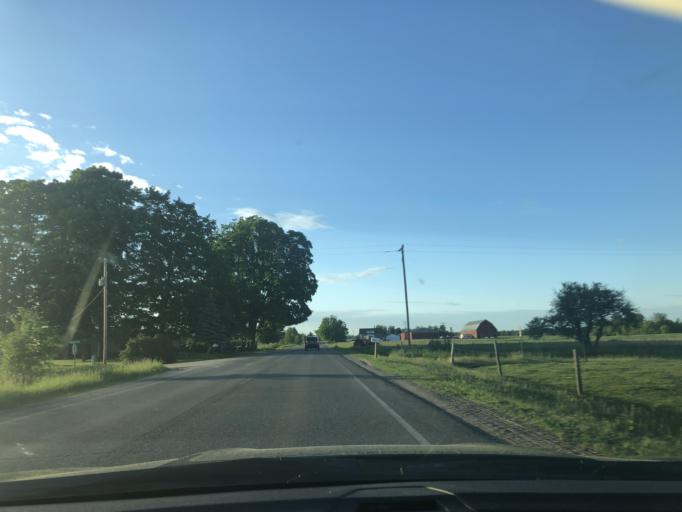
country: US
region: Michigan
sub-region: Missaukee County
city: Lake City
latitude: 44.4225
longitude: -85.0753
